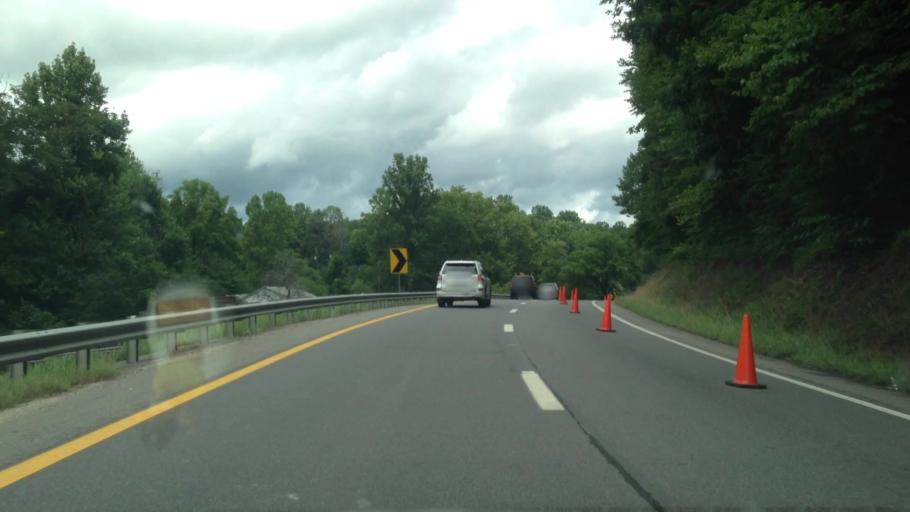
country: US
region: Virginia
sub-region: Henry County
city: Stanleytown
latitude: 36.7632
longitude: -79.9375
